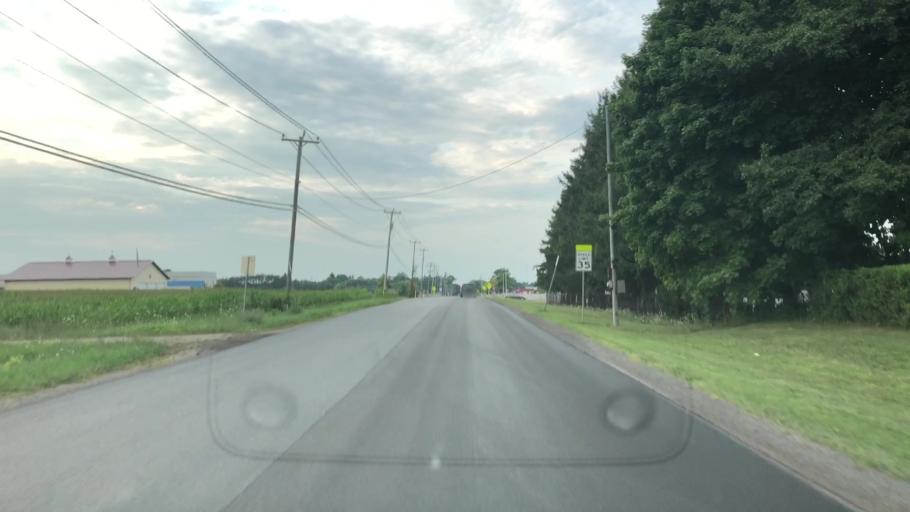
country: US
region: New York
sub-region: Erie County
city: Elma Center
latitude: 42.8310
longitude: -78.6060
